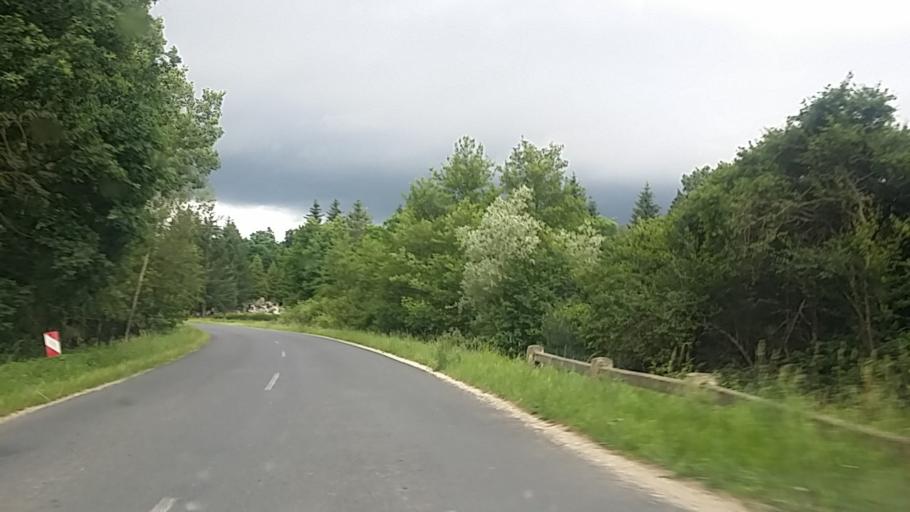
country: SI
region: Hodos-Hodos
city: Hodos
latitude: 46.8463
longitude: 16.4104
